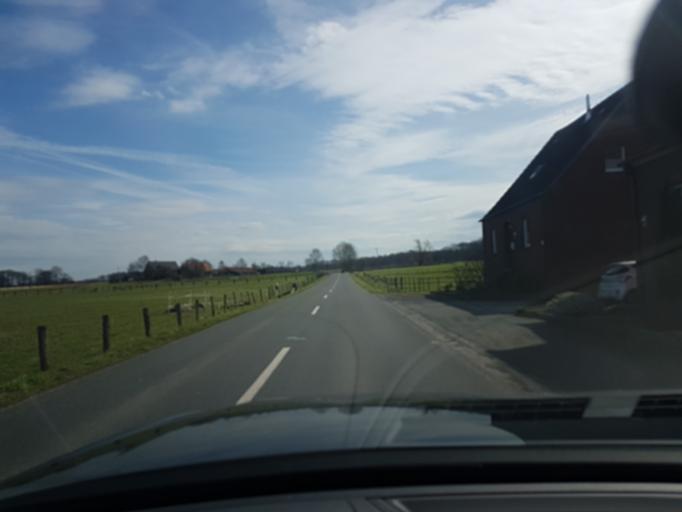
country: DE
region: North Rhine-Westphalia
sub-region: Regierungsbezirk Munster
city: Nordkirchen
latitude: 51.6988
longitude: 7.5549
